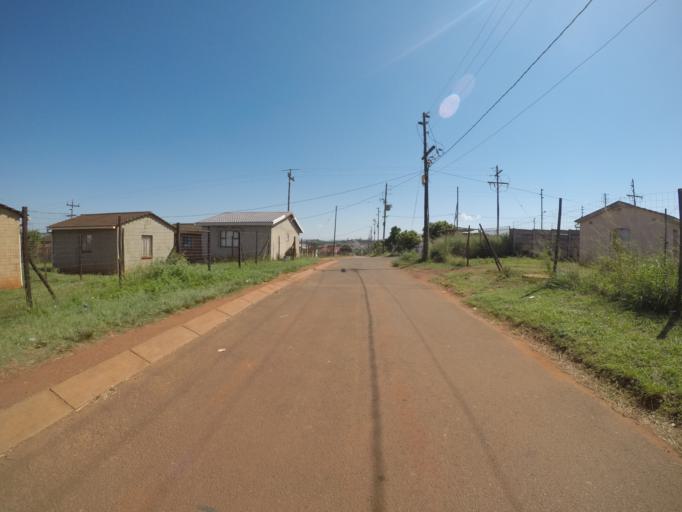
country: ZA
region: KwaZulu-Natal
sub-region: uThungulu District Municipality
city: Empangeni
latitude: -28.7715
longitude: 31.8779
